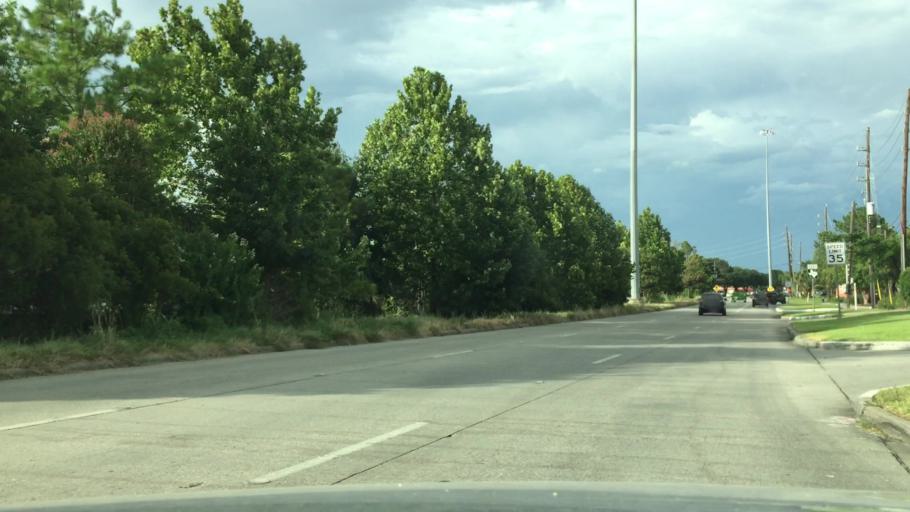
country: US
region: Texas
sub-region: Harris County
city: Hudson
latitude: 29.9611
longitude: -95.5466
